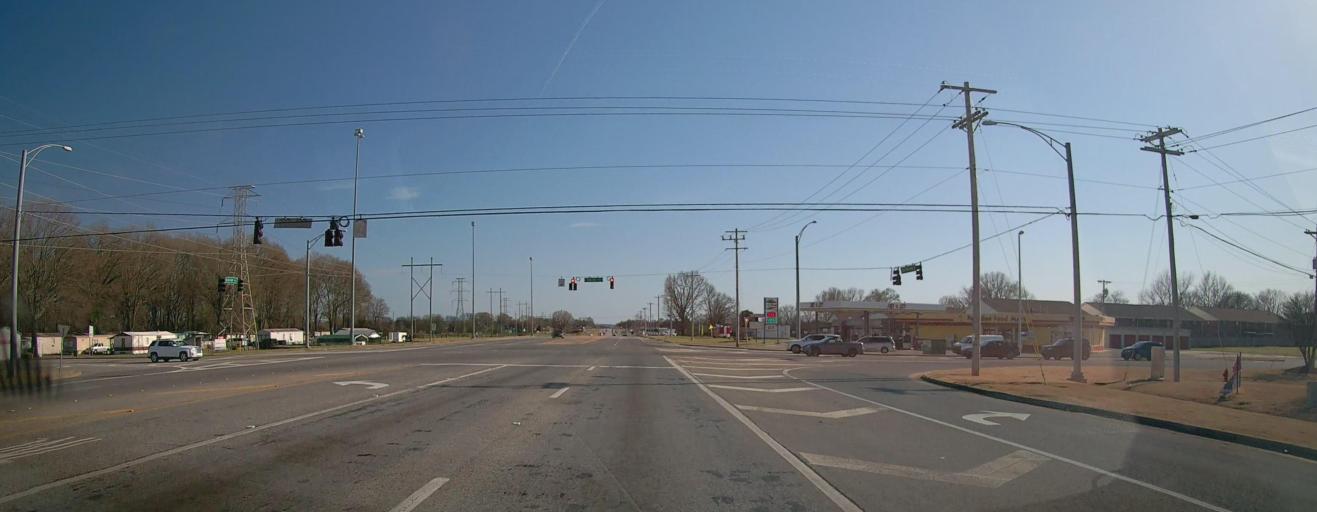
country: US
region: Alabama
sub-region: Colbert County
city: Muscle Shoals
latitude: 34.7448
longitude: -87.6354
